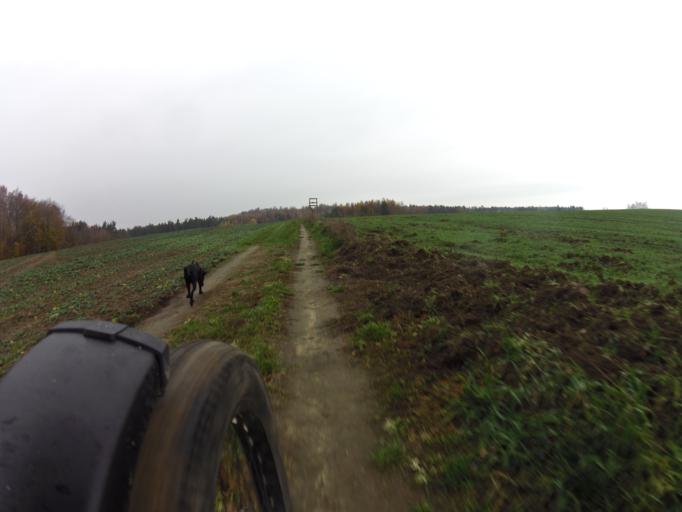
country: PL
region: Pomeranian Voivodeship
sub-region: Powiat pucki
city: Krokowa
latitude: 54.7269
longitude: 18.1319
